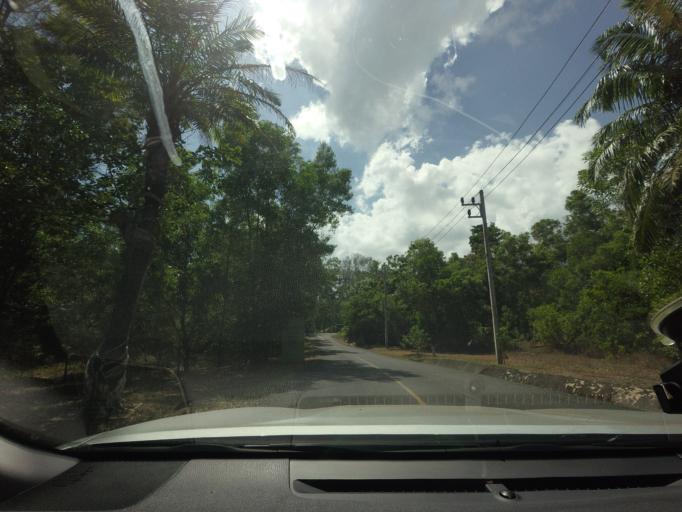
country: TH
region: Phuket
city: Mueang Phuket
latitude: 7.8744
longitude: 98.3549
